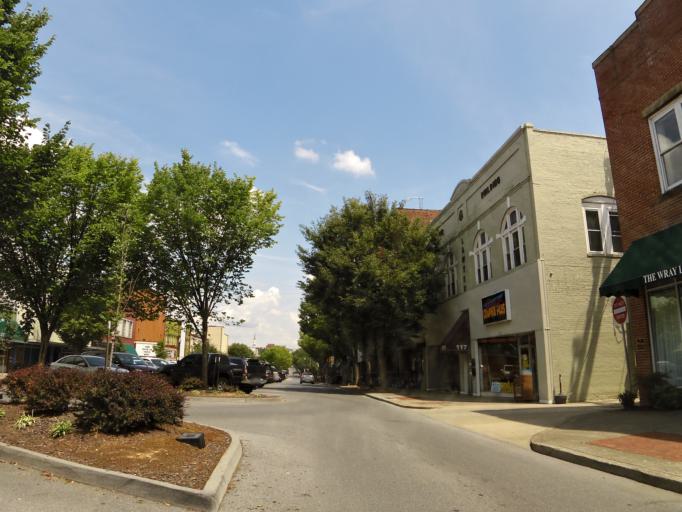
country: US
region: Tennessee
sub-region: Sullivan County
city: Kingsport
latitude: 36.5454
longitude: -82.5618
